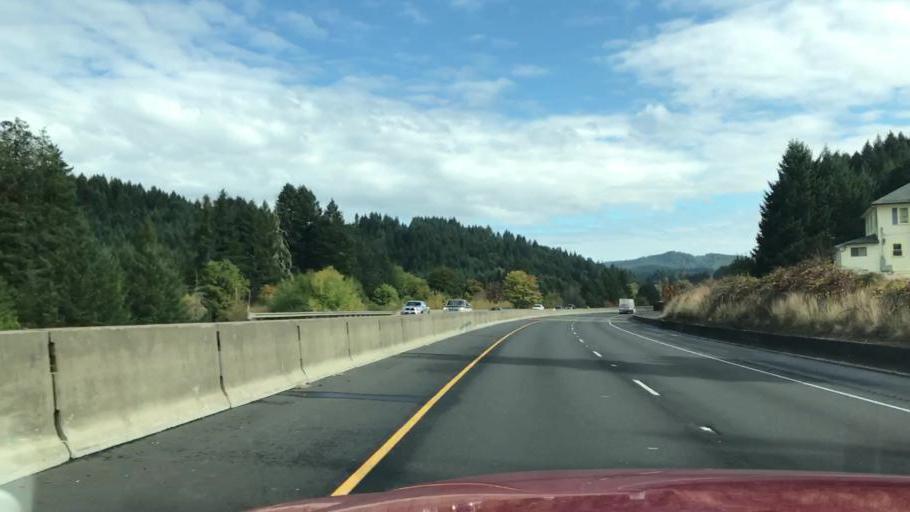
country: US
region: Oregon
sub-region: Douglas County
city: Drain
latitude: 43.7327
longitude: -123.1979
